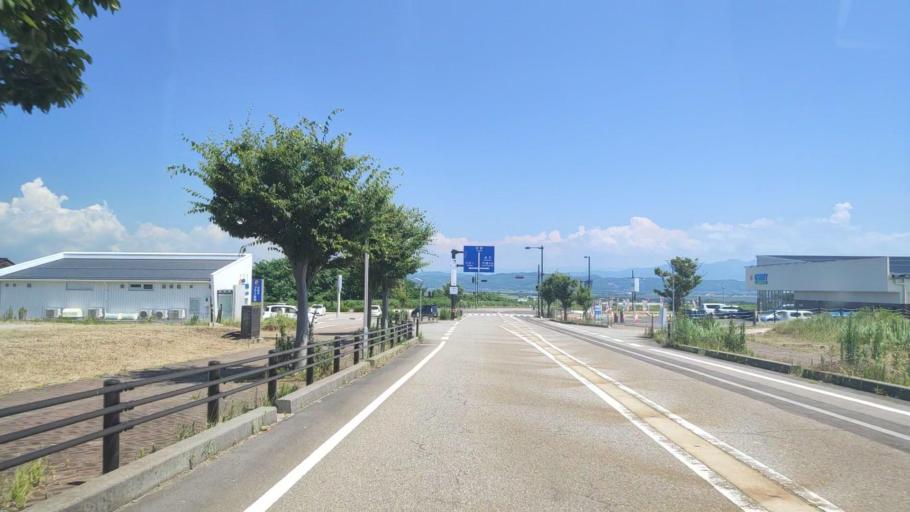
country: JP
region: Ishikawa
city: Tsubata
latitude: 36.6718
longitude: 136.6576
